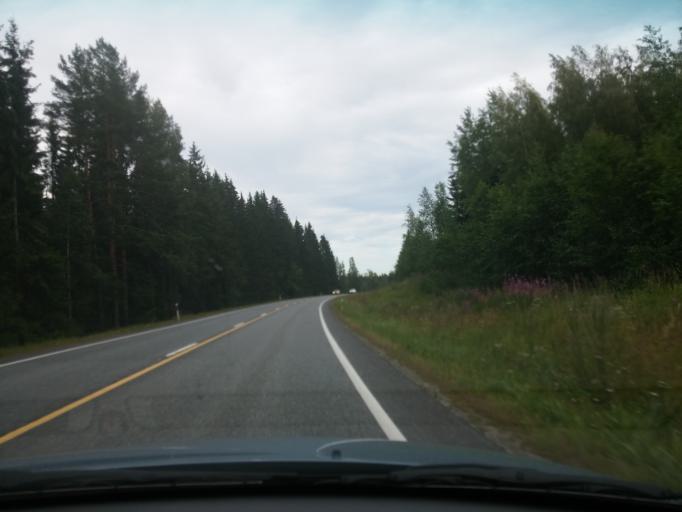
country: FI
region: Haeme
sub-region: Haemeenlinna
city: Tervakoski
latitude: 60.7449
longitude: 24.6632
